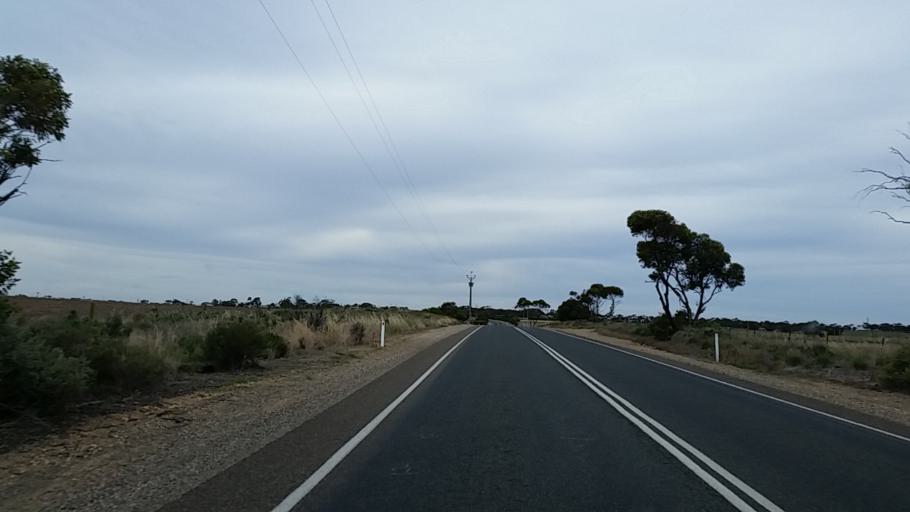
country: AU
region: South Australia
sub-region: Mid Murray
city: Mannum
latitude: -34.9086
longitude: 139.2758
